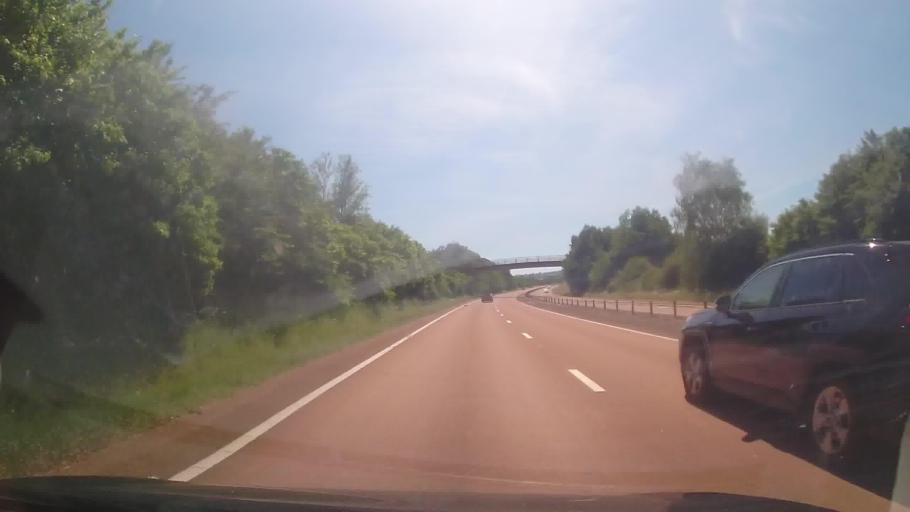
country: GB
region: England
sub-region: Devon
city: Ottery St Mary
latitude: 50.7766
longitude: -3.2730
